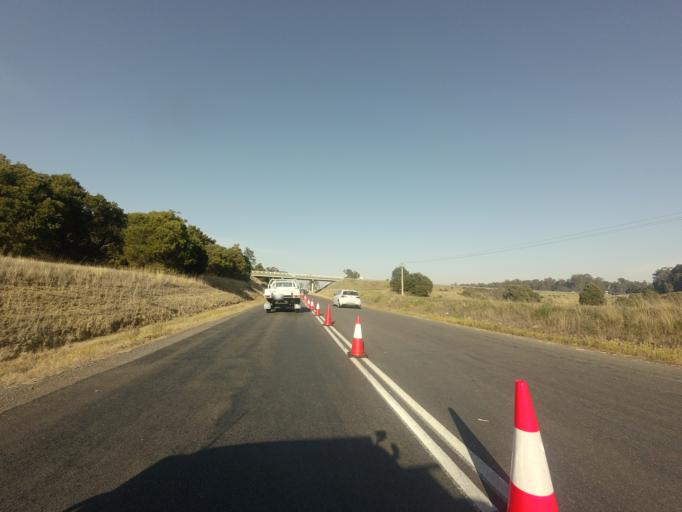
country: AU
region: Tasmania
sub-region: Northern Midlands
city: Longford
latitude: -41.5523
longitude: 146.9894
